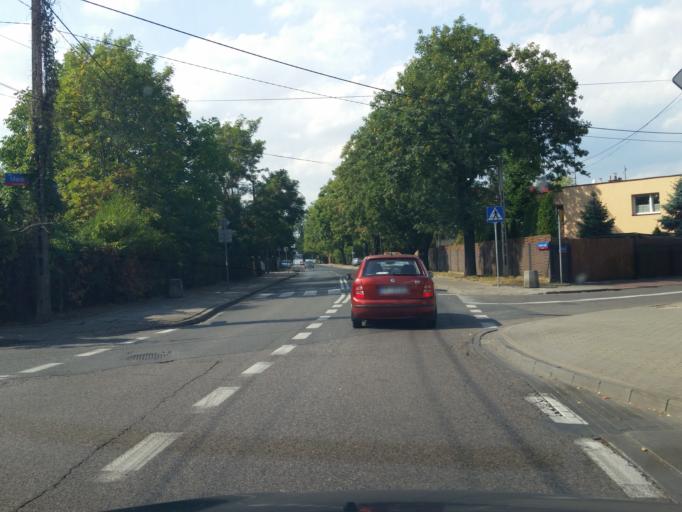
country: PL
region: Masovian Voivodeship
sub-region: Warszawa
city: Ursus
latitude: 52.1977
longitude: 20.8786
